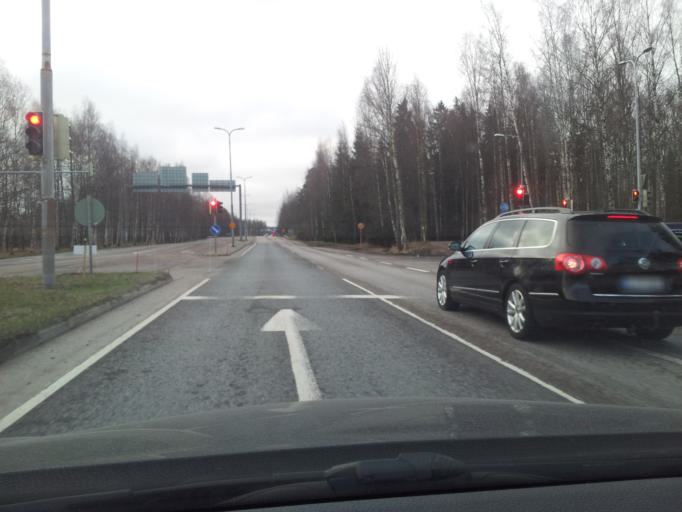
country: FI
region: Uusimaa
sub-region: Helsinki
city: Teekkarikylae
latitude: 60.2315
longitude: 24.8658
